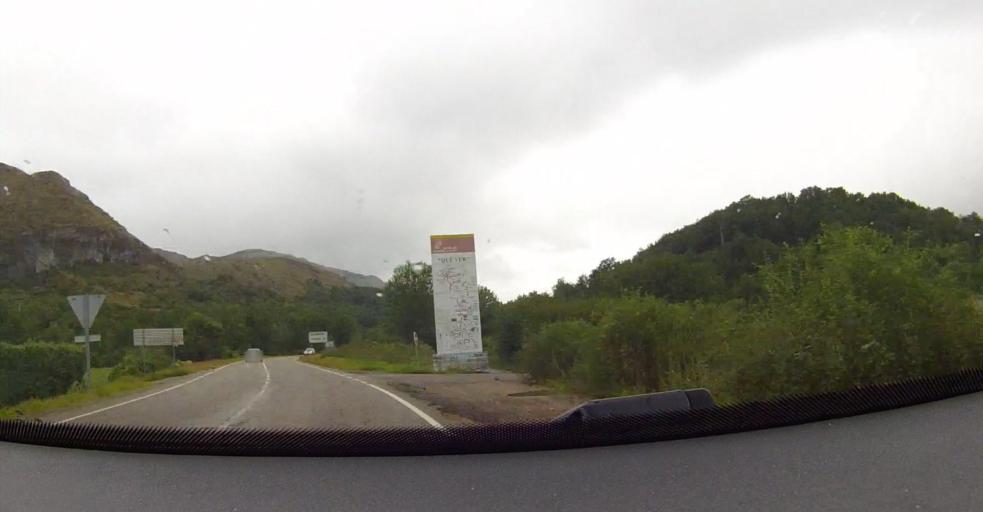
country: ES
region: Castille and Leon
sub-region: Provincia de Leon
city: Sabero
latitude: 42.8327
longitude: -5.1288
